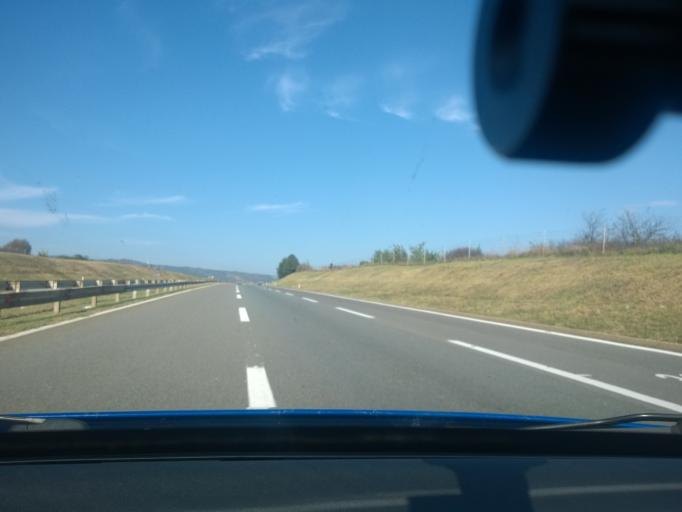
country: RS
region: Central Serbia
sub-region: Nisavski Okrug
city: Razanj
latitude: 43.6349
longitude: 21.5618
